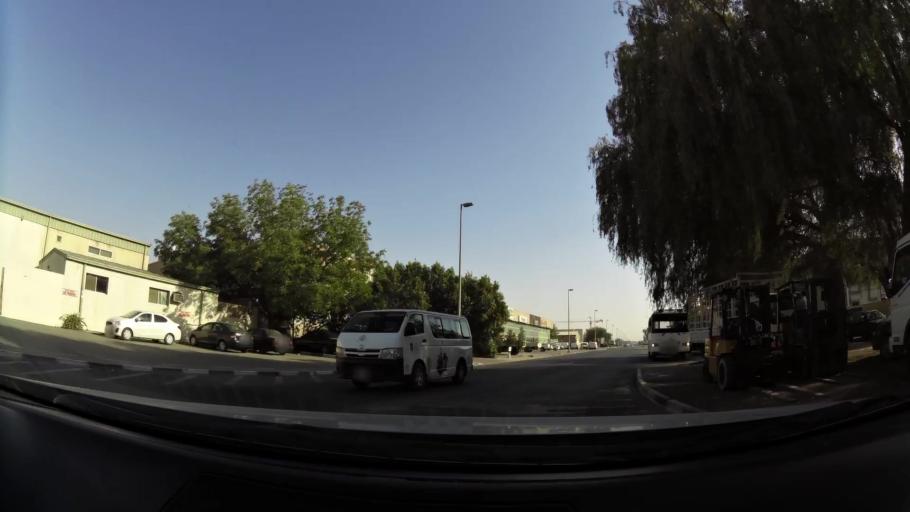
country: AE
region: Dubai
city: Dubai
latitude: 25.1185
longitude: 55.2360
